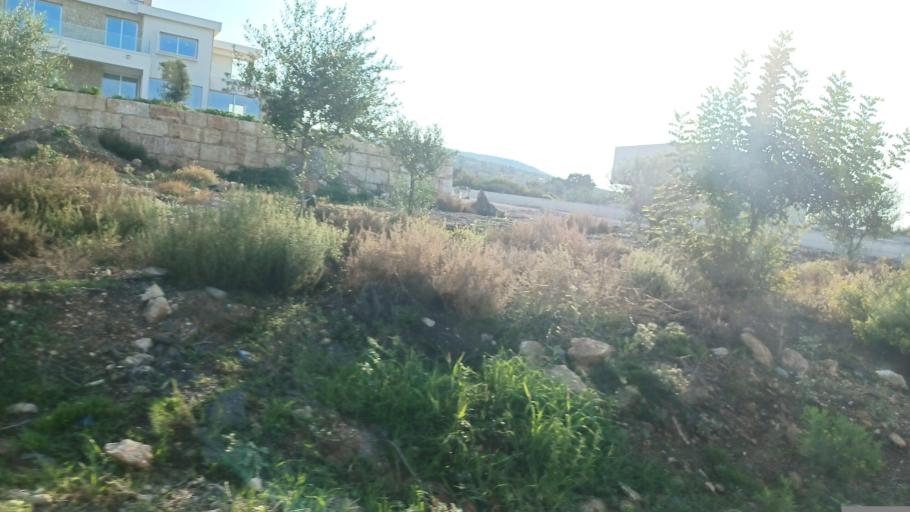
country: CY
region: Pafos
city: Pegeia
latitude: 34.9044
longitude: 32.3327
